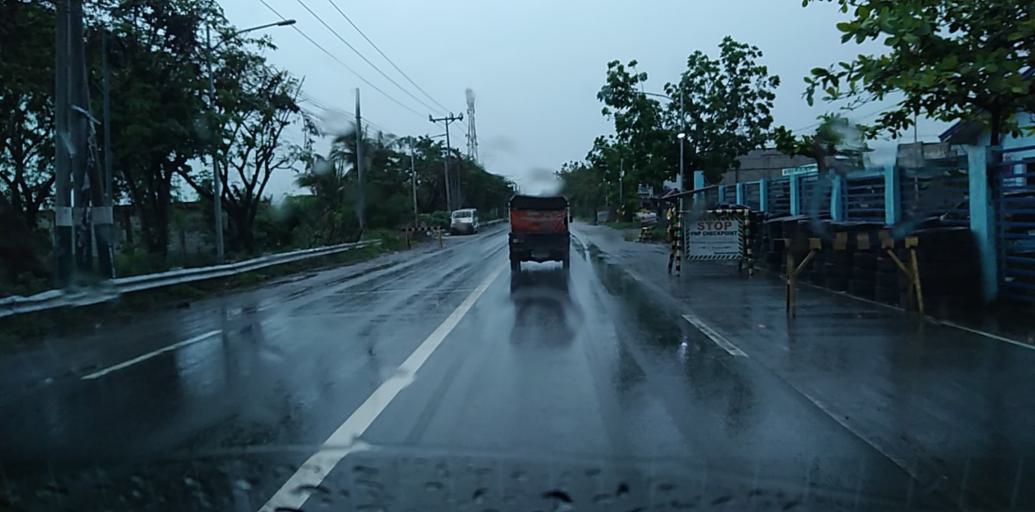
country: PH
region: Central Luzon
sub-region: Province of Bulacan
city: Bulualto
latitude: 15.2153
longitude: 120.9550
